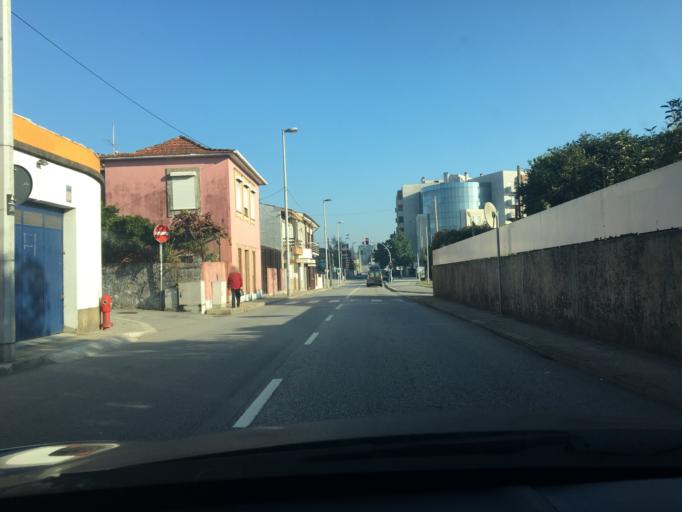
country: PT
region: Porto
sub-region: Maia
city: Maia
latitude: 41.2377
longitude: -8.6218
